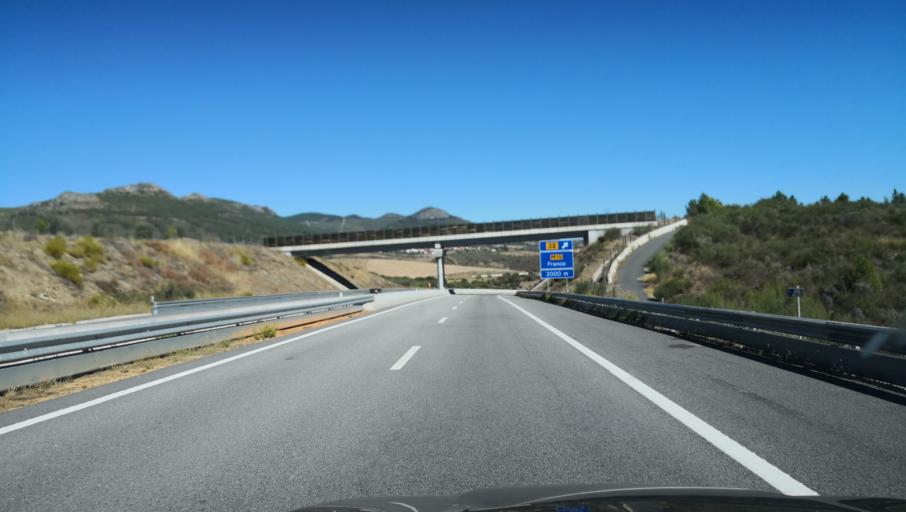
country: PT
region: Vila Real
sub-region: Murca
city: Murca
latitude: 41.4218
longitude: -7.3699
